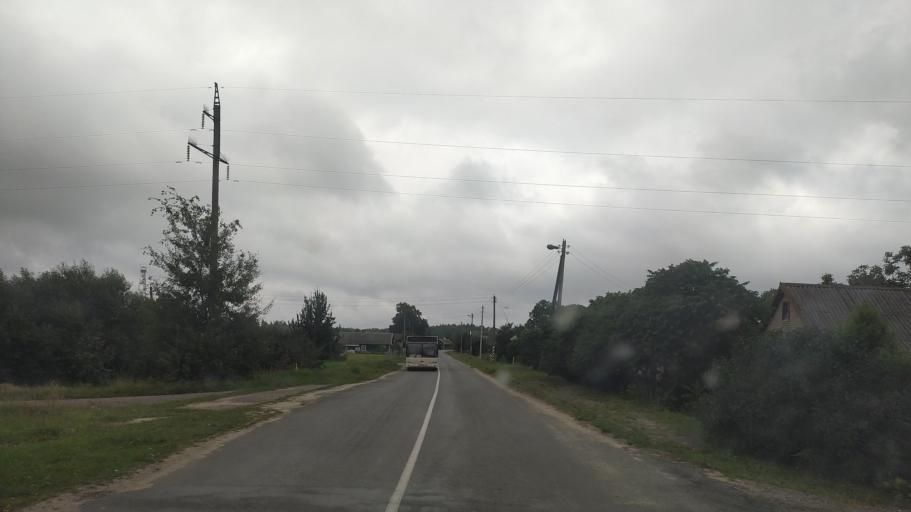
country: BY
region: Brest
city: Byaroza
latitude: 52.5930
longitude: 24.8710
